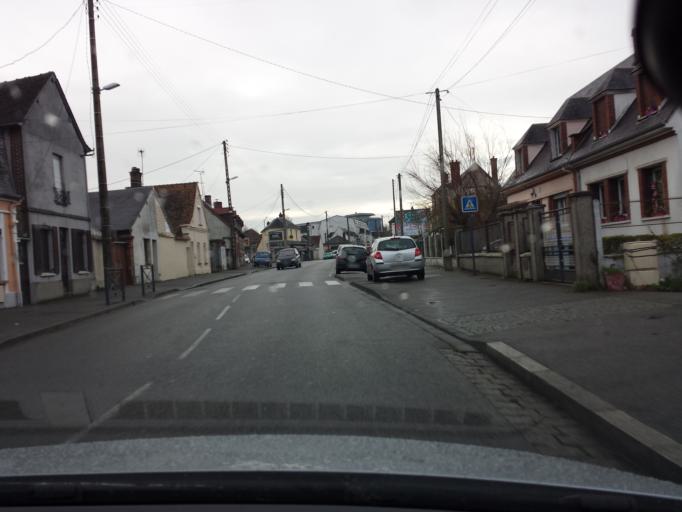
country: FR
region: Haute-Normandie
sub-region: Departement de l'Eure
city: Evreux
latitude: 49.0121
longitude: 1.1523
